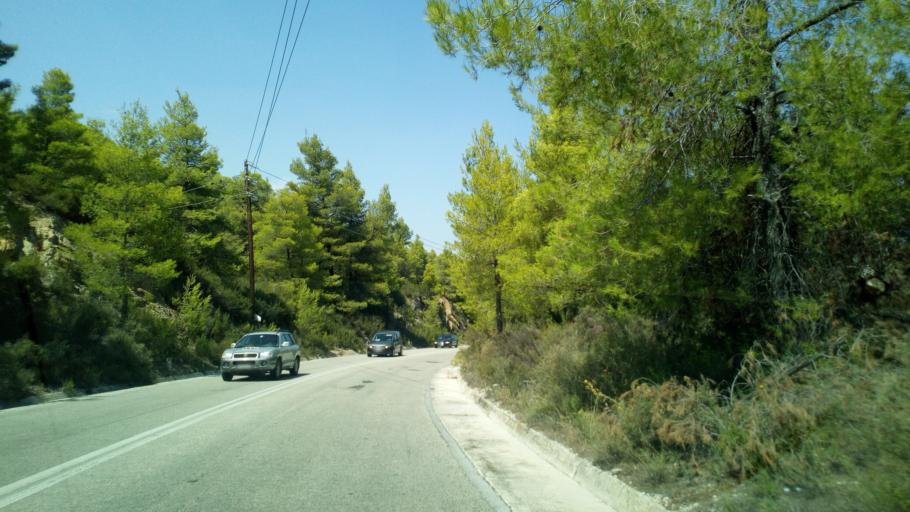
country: GR
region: Central Macedonia
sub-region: Nomos Chalkidikis
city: Sarti
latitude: 40.1465
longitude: 23.9192
